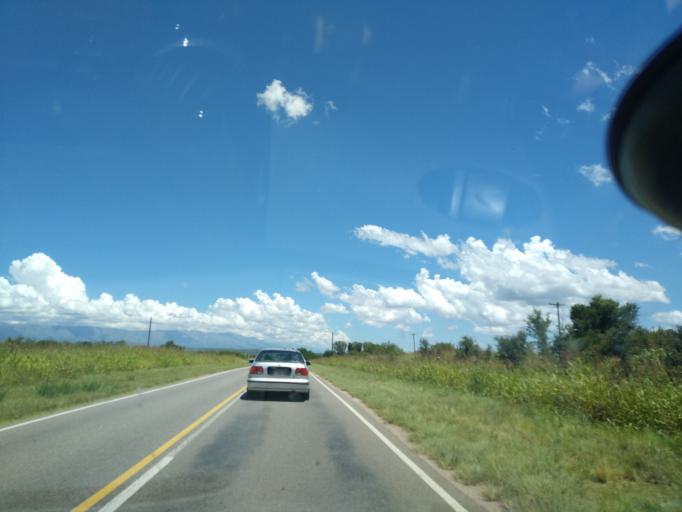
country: AR
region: Cordoba
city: Villa Cura Brochero
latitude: -31.6225
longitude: -65.1087
